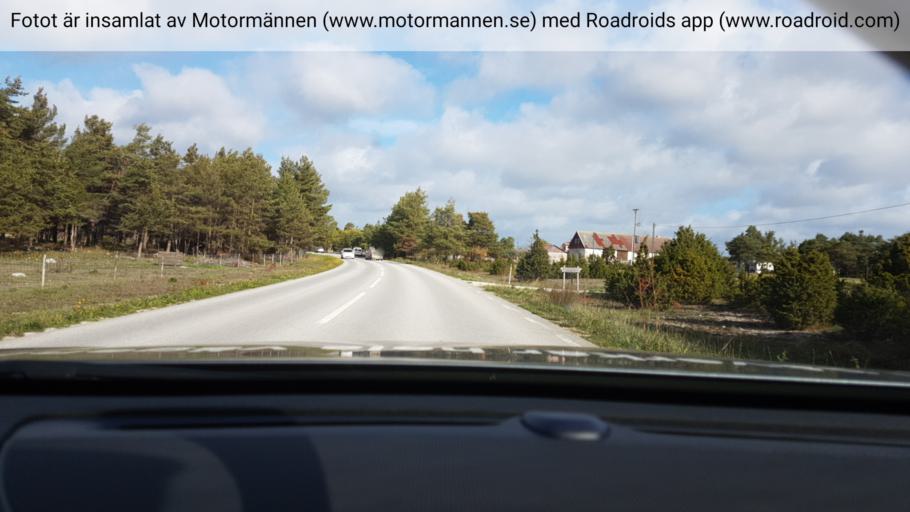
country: SE
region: Gotland
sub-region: Gotland
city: Slite
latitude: 57.8935
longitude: 19.0928
